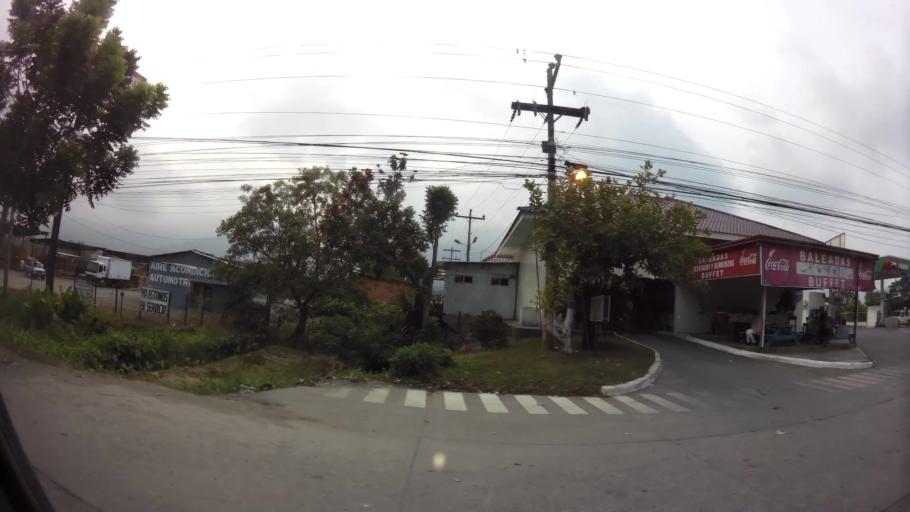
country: HN
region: Yoro
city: El Progreso
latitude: 15.4155
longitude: -87.8021
